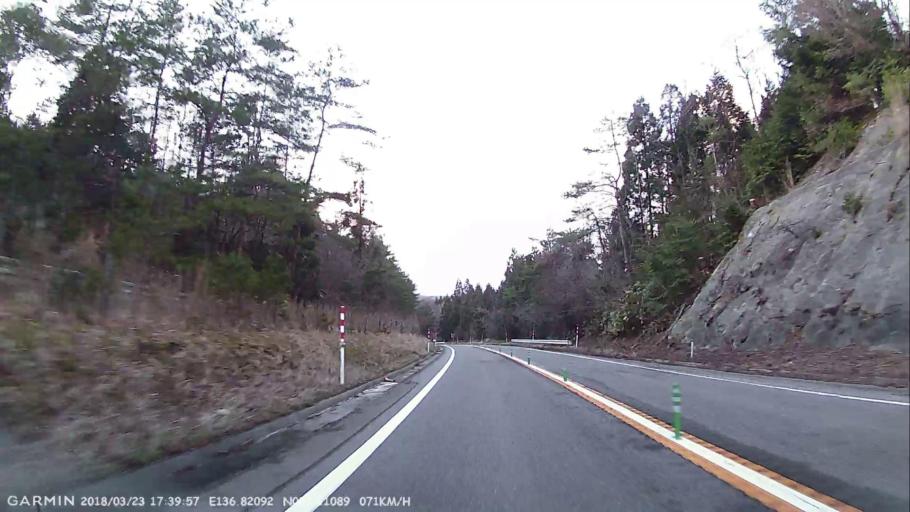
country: JP
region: Ishikawa
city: Nanao
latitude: 37.1112
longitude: 136.8208
